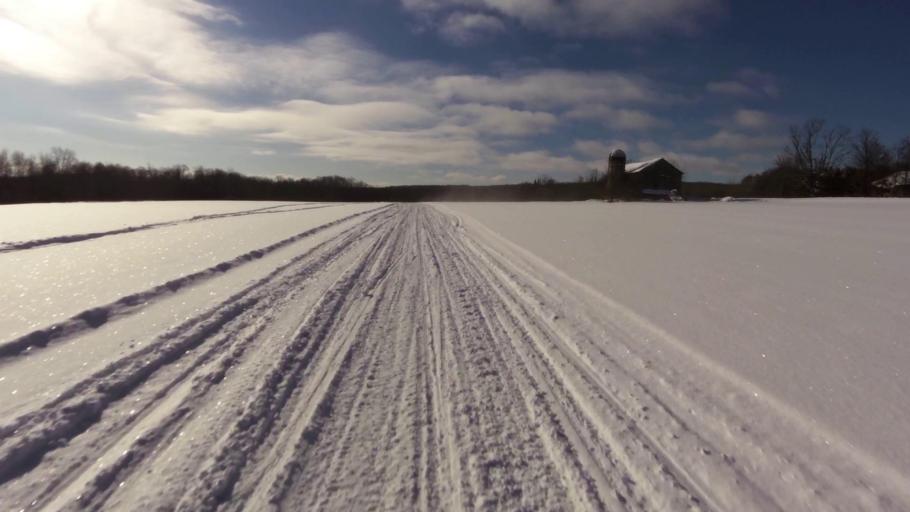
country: US
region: New York
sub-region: Chautauqua County
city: Falconer
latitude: 42.2679
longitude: -79.1133
